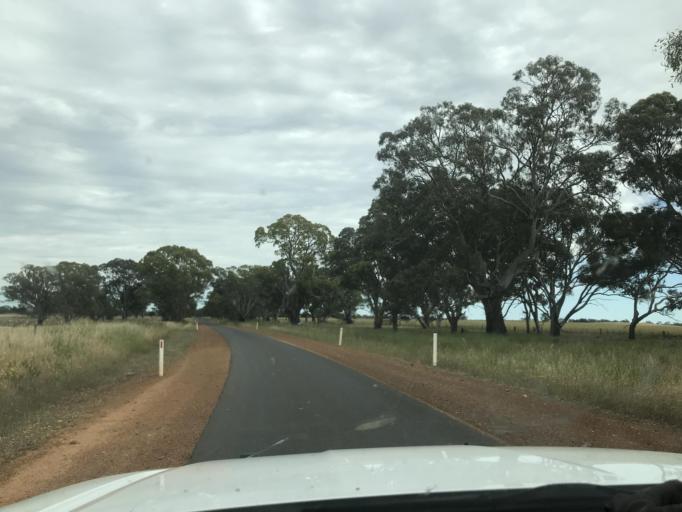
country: AU
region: Victoria
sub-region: Horsham
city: Horsham
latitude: -36.9826
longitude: 141.5417
